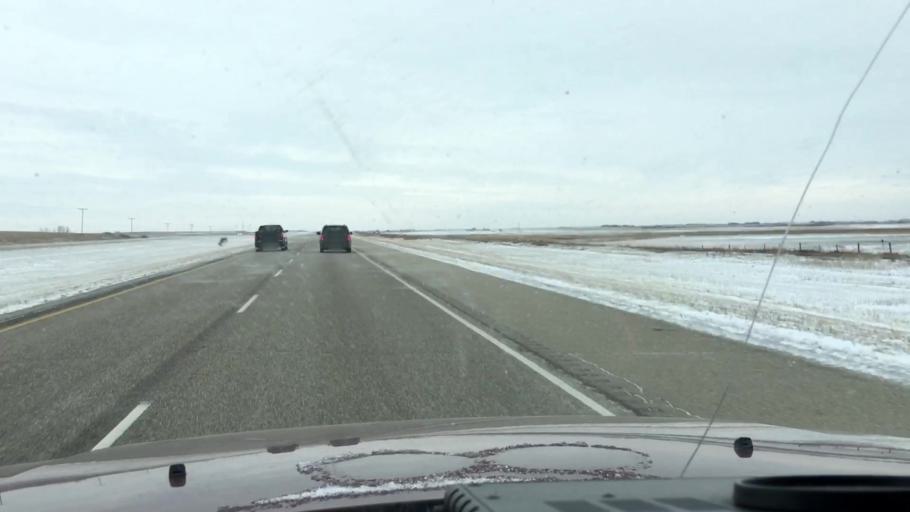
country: CA
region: Saskatchewan
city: Saskatoon
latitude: 51.5984
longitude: -106.3931
